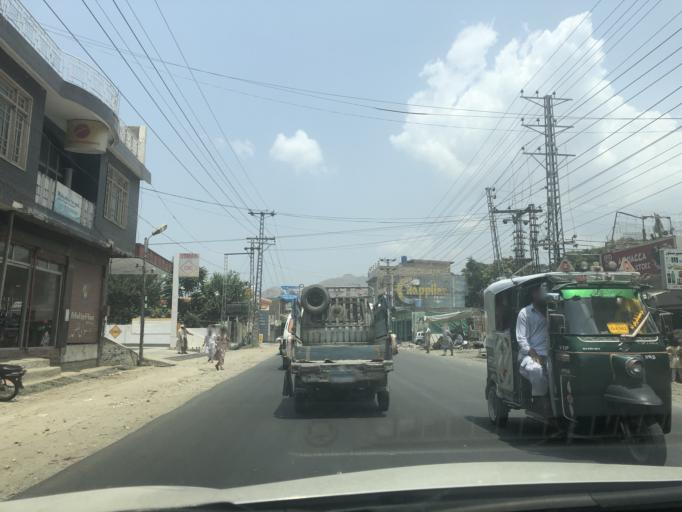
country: PK
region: Khyber Pakhtunkhwa
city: Mingora
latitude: 34.7706
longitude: 72.3443
